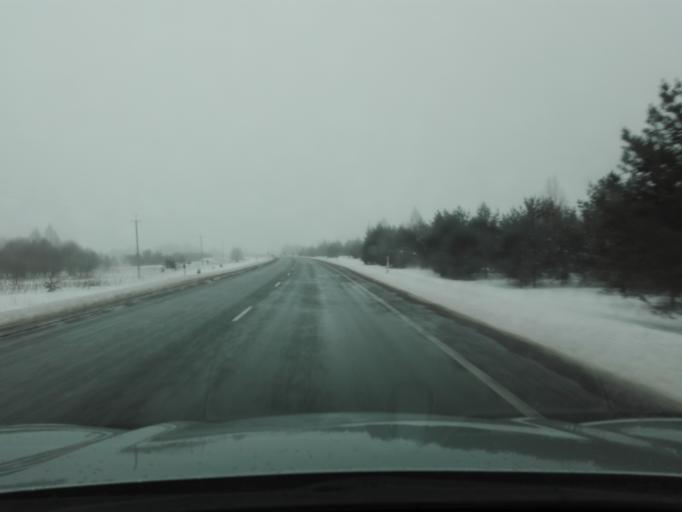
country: EE
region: Raplamaa
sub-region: Kohila vald
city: Kohila
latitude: 59.1229
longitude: 24.7893
